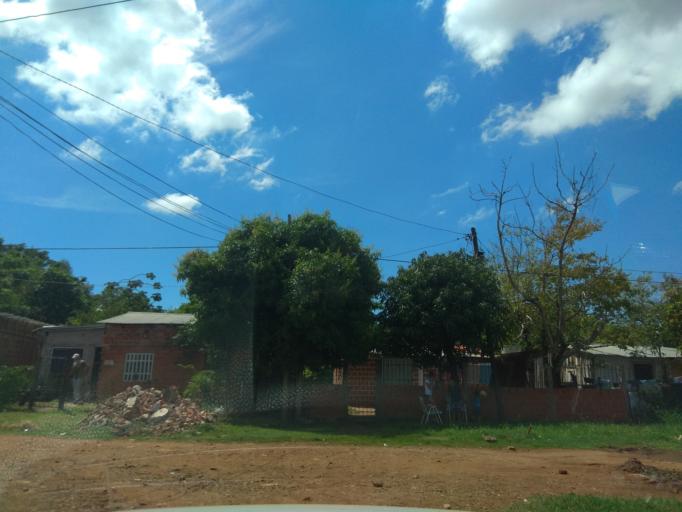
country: AR
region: Misiones
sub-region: Departamento de Capital
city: Posadas
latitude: -27.3873
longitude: -55.9239
